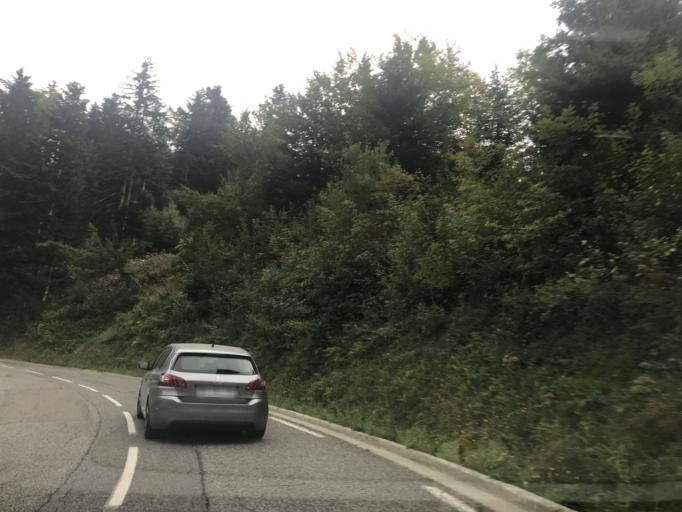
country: ES
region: Catalonia
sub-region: Provincia de Lleida
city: Les
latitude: 42.7704
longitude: 0.6602
